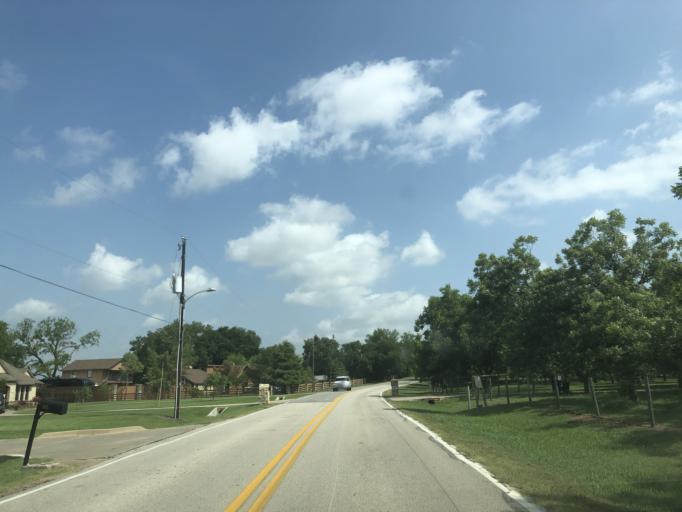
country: US
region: Texas
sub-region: Dallas County
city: Sunnyvale
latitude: 32.8250
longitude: -96.5597
